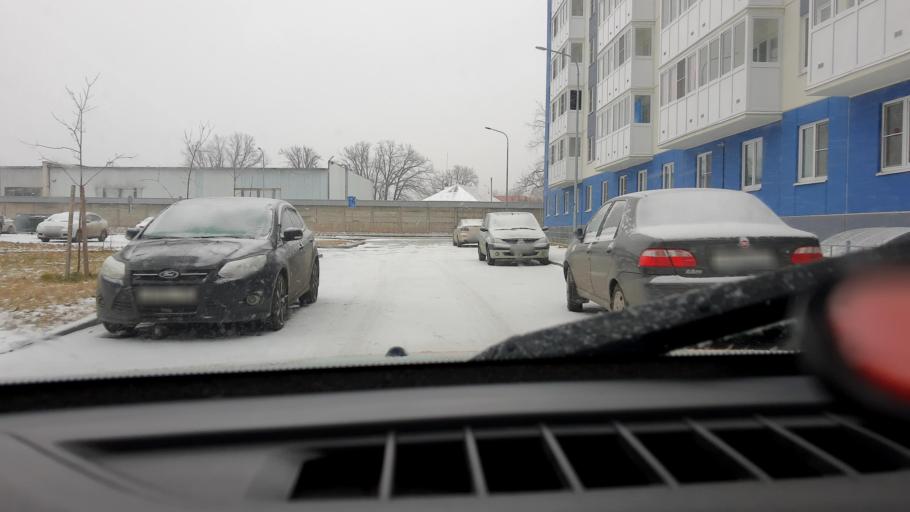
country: RU
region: Nizjnij Novgorod
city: Burevestnik
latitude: 56.2085
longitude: 43.8215
